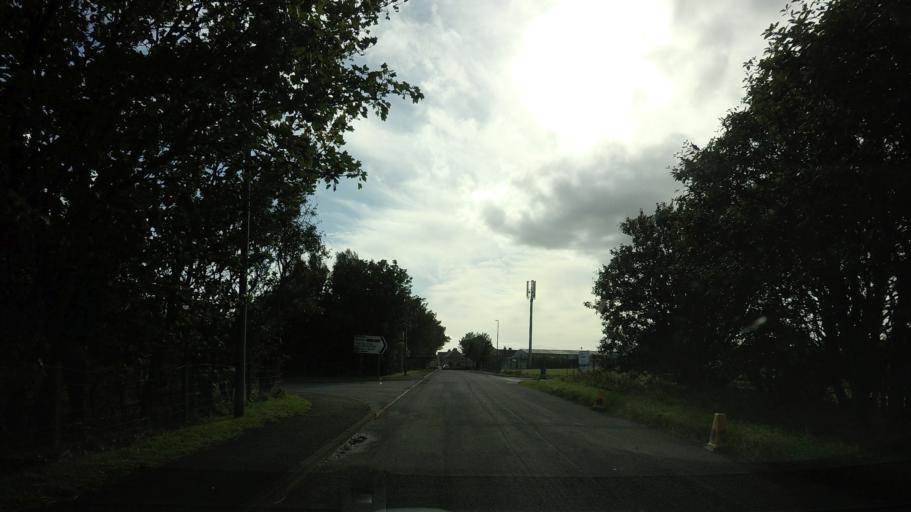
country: GB
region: Scotland
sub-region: Highland
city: Wick
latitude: 58.4494
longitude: -3.0884
